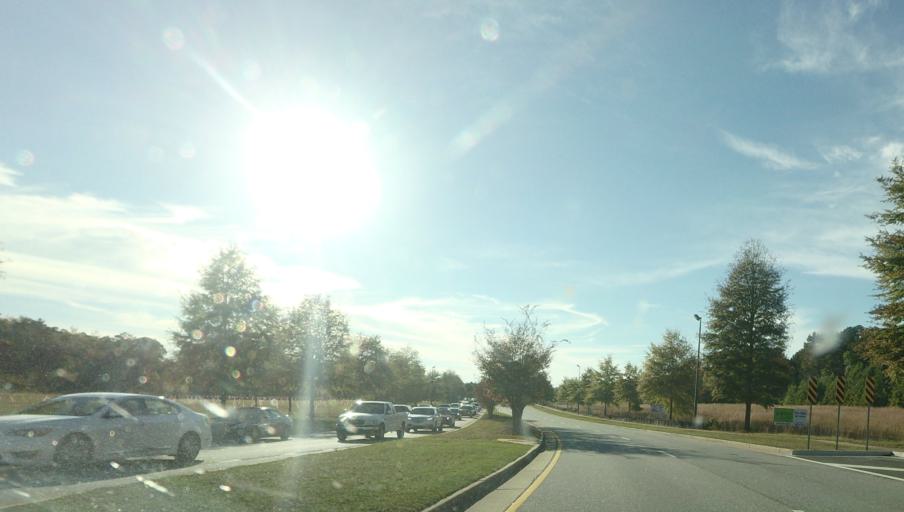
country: US
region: Alabama
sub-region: Russell County
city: Phenix City
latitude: 32.5506
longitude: -84.9312
